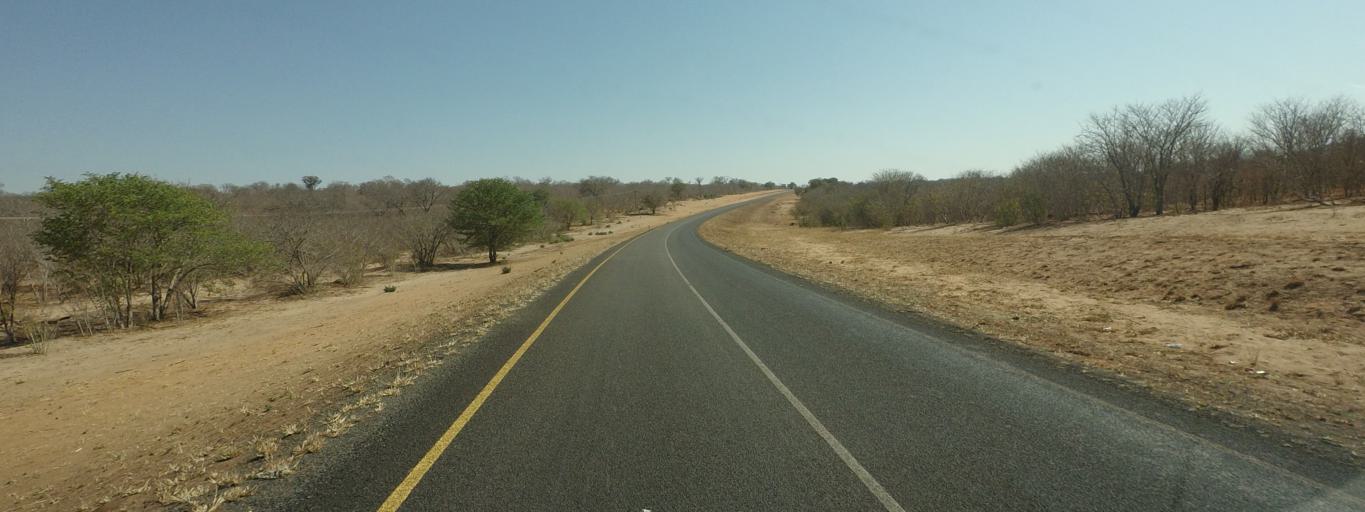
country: BW
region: North West
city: Kasane
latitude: -17.8775
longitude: 25.2127
